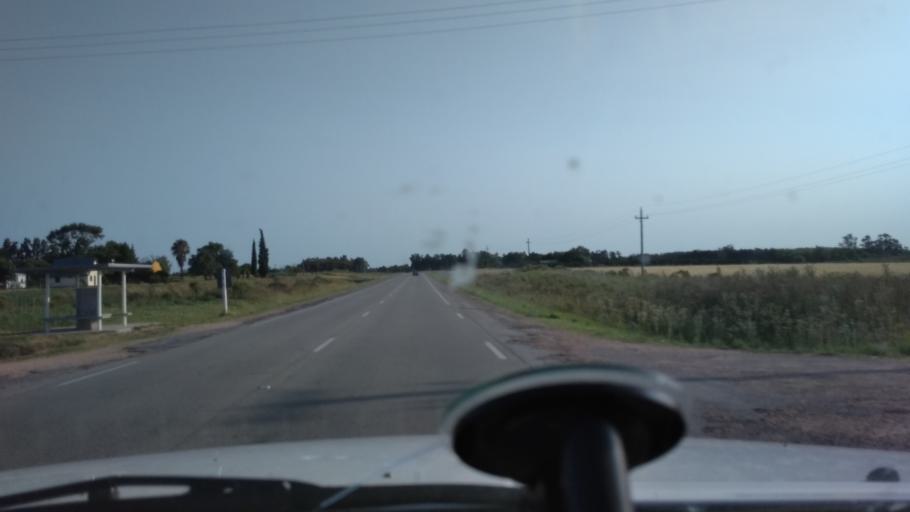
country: UY
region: Canelones
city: Santa Rosa
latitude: -34.5689
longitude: -56.0562
